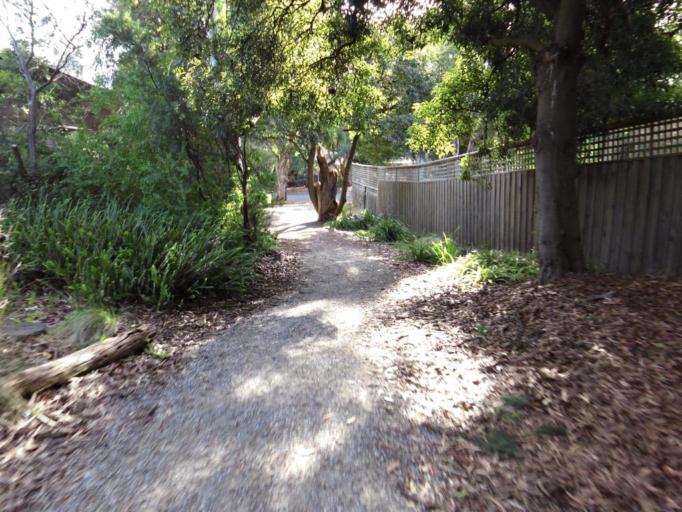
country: AU
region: Victoria
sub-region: Whitehorse
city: Blackburn
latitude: -37.8204
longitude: 145.1454
